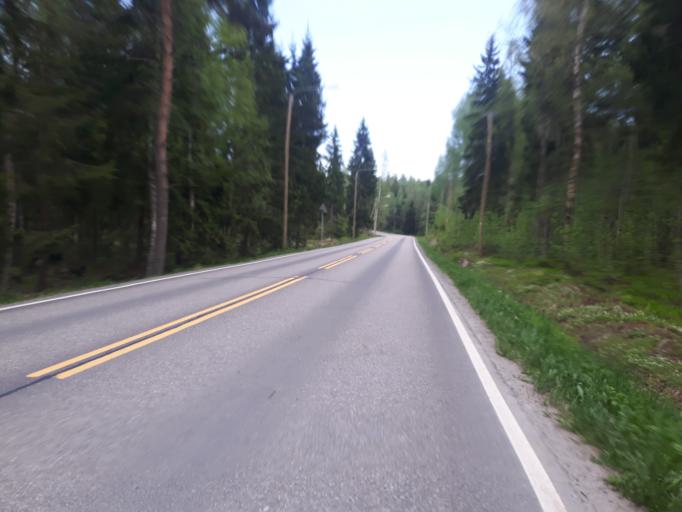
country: FI
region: Uusimaa
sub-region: Porvoo
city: Porvoo
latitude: 60.3900
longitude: 25.7487
